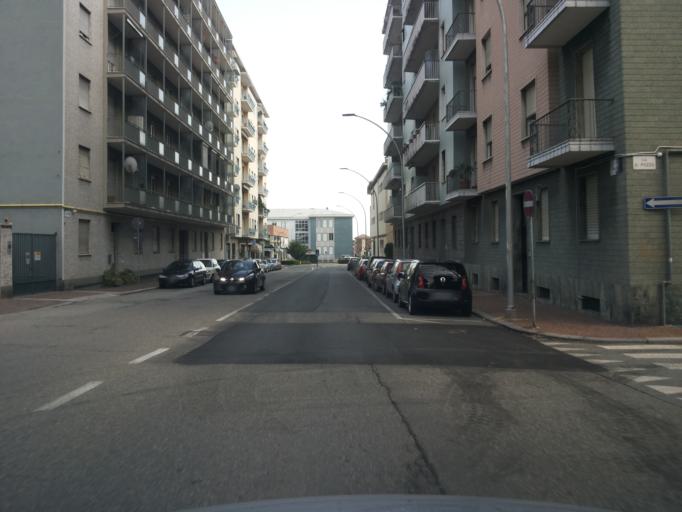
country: IT
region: Piedmont
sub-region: Provincia di Biella
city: Biella
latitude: 45.5607
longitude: 8.0518
